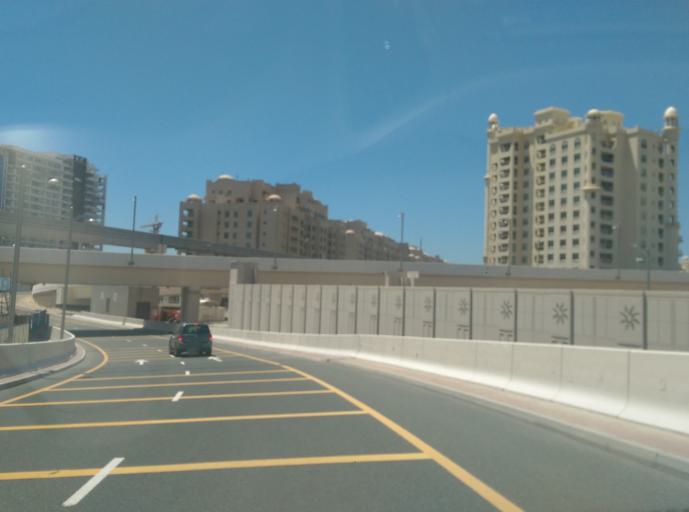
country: AE
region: Dubai
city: Dubai
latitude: 25.1048
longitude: 55.1516
